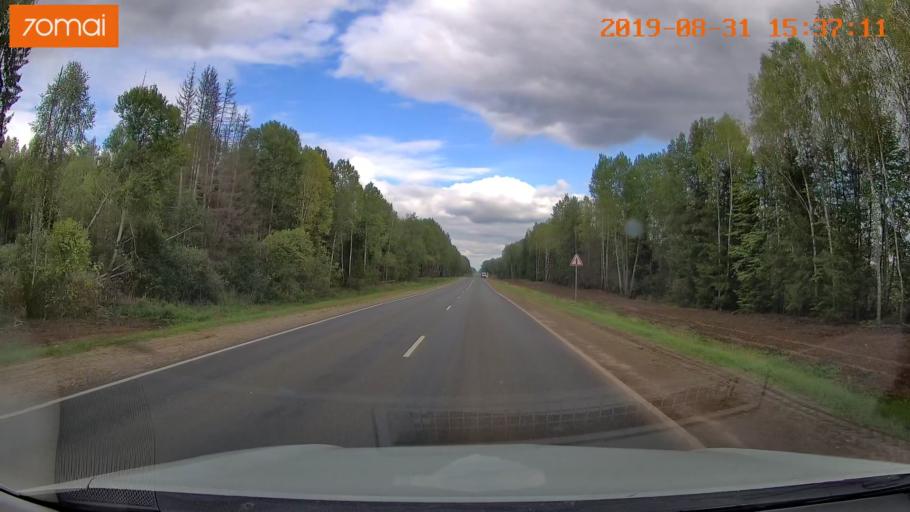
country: RU
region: Kaluga
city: Mosal'sk
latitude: 54.6165
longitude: 34.7780
